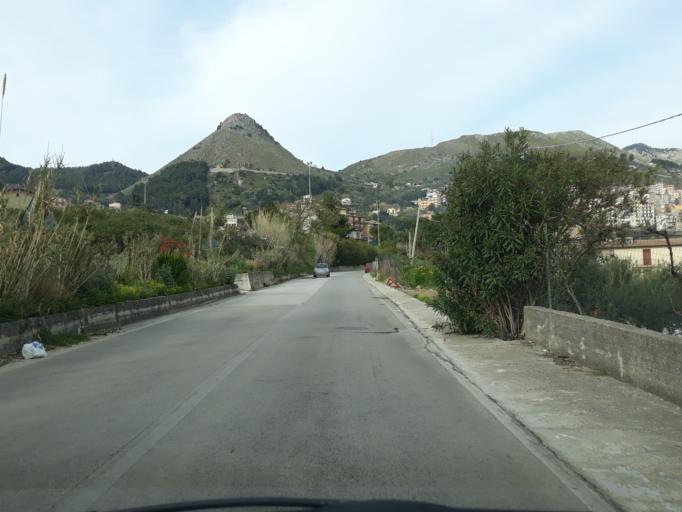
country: IT
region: Sicily
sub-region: Palermo
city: Giardinello
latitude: 38.0854
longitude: 13.1639
